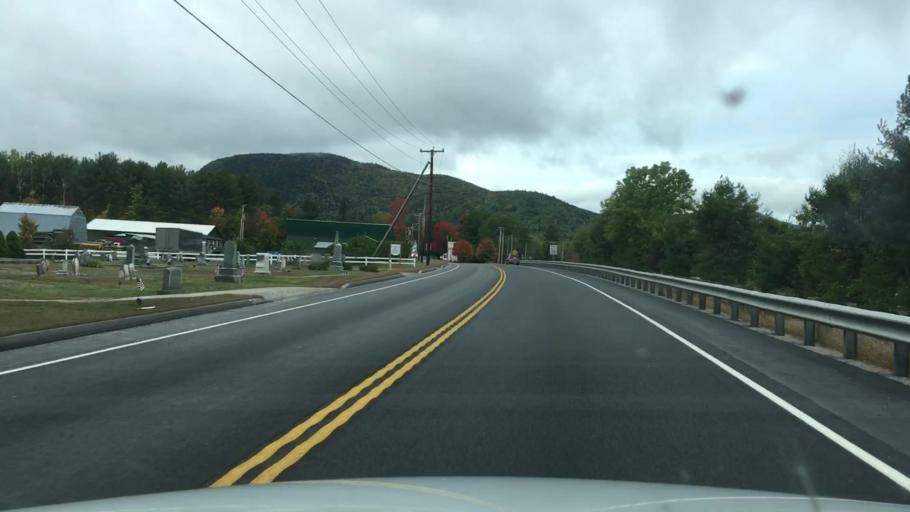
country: US
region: Maine
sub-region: Oxford County
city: Bethel
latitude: 44.4059
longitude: -70.8561
